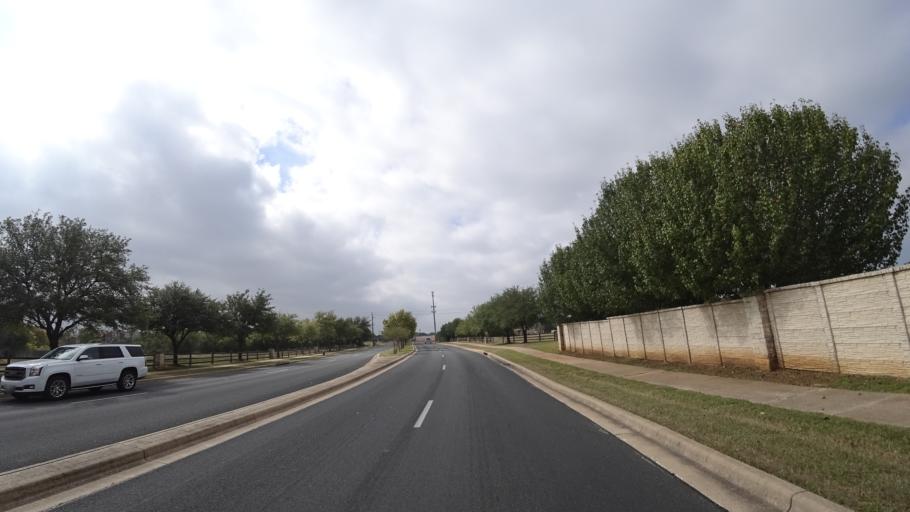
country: US
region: Texas
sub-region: Travis County
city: Shady Hollow
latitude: 30.1839
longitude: -97.8385
